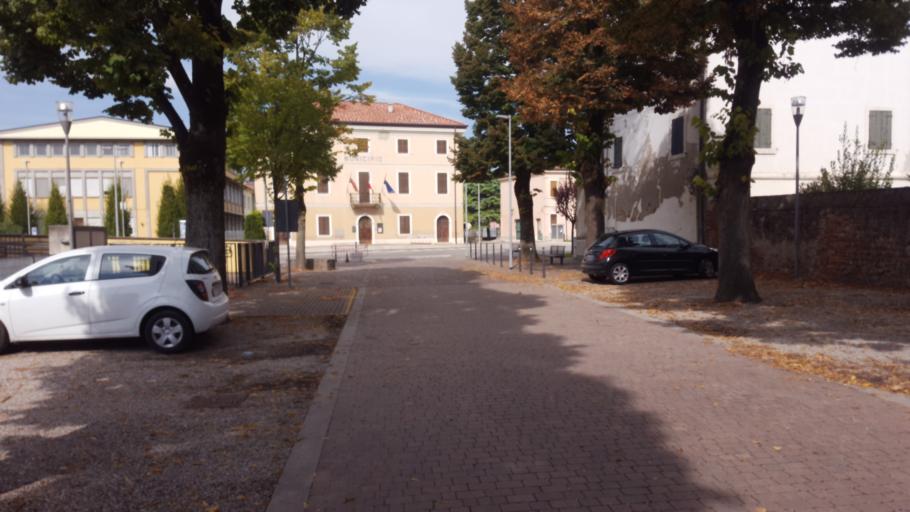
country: IT
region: Veneto
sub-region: Provincia di Verona
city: Salizzole
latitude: 45.2422
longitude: 11.0845
